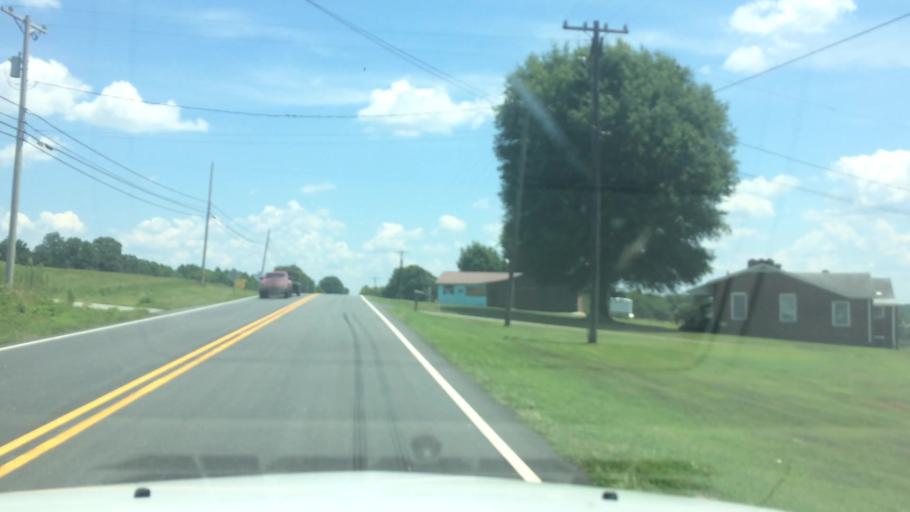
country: US
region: North Carolina
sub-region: Alexander County
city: Taylorsville
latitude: 35.9196
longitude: -81.2277
